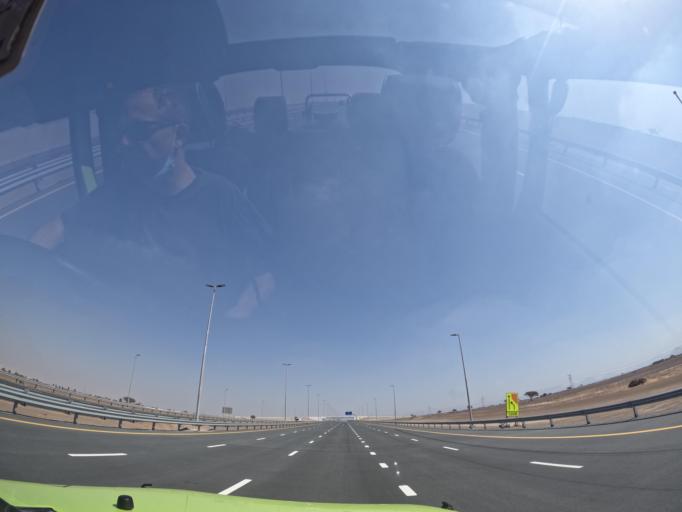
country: AE
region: Ash Shariqah
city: Adh Dhayd
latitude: 24.9262
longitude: 55.8100
